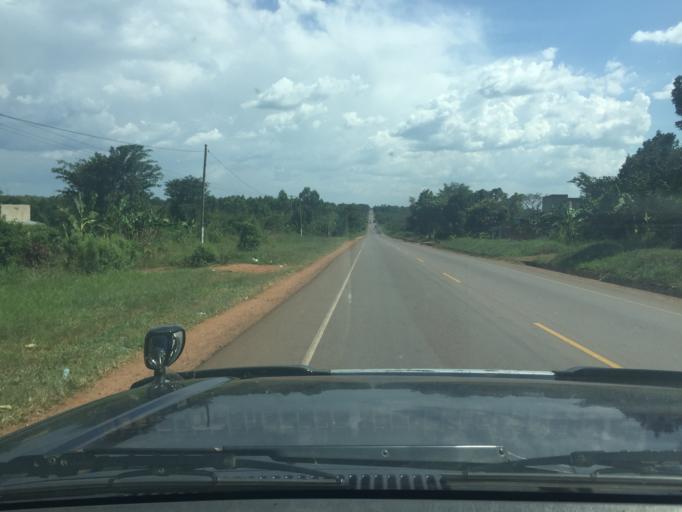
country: UG
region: Central Region
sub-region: Luwero District
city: Luwero
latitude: 0.7964
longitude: 32.5078
